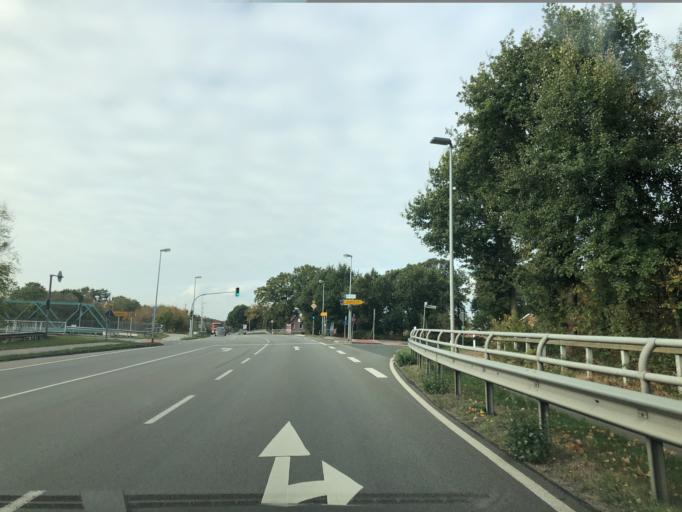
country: DE
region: Lower Saxony
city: Edewecht
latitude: 53.0901
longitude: 8.0571
